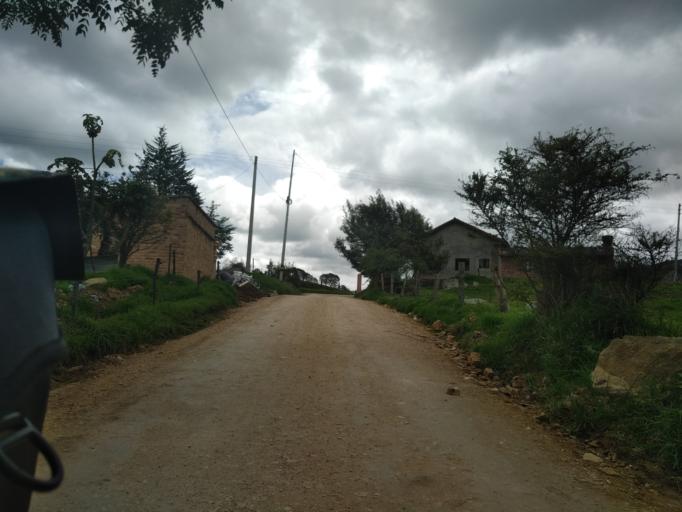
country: CO
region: Cundinamarca
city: Lenguazaque
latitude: 5.2933
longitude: -73.7193
